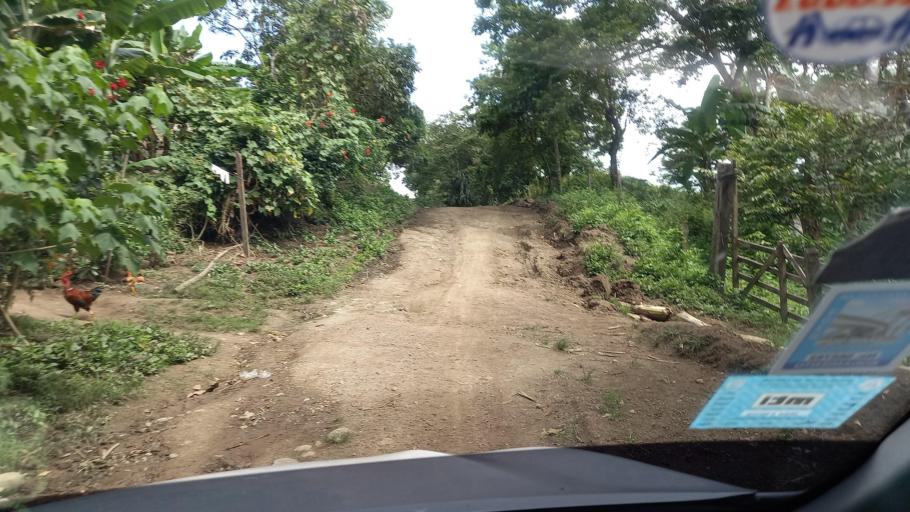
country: NI
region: Jinotega
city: San Jose de Bocay
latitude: 13.4039
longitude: -85.7012
